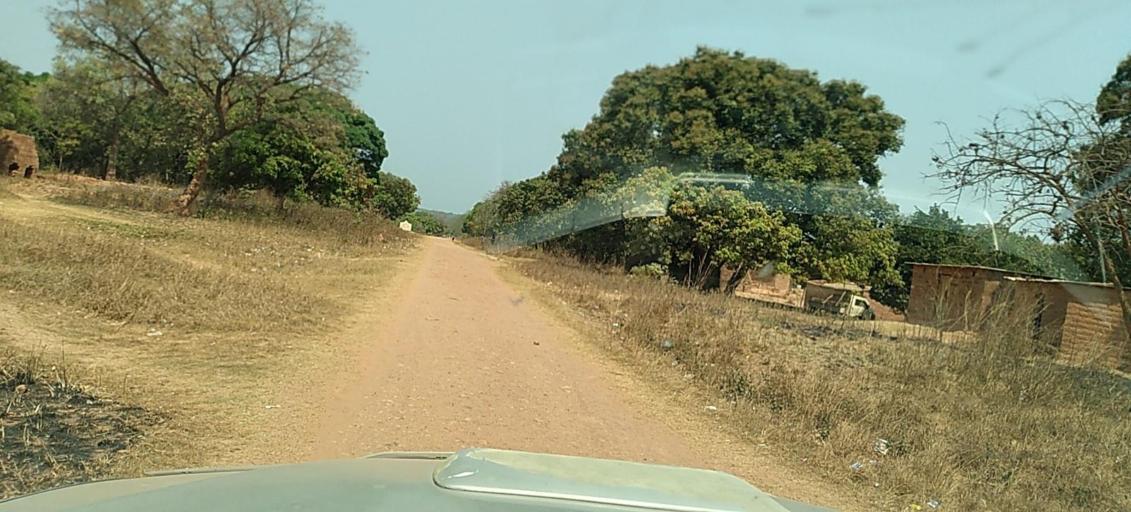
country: ZM
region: North-Western
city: Kasempa
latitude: -13.7064
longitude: 26.3354
